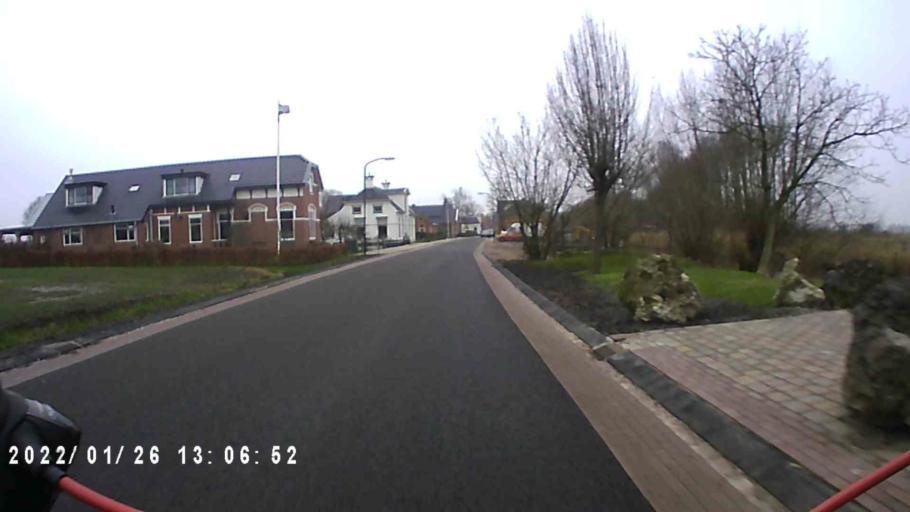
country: NL
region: Groningen
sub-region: Gemeente Zuidhorn
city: Oldehove
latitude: 53.3560
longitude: 6.4325
